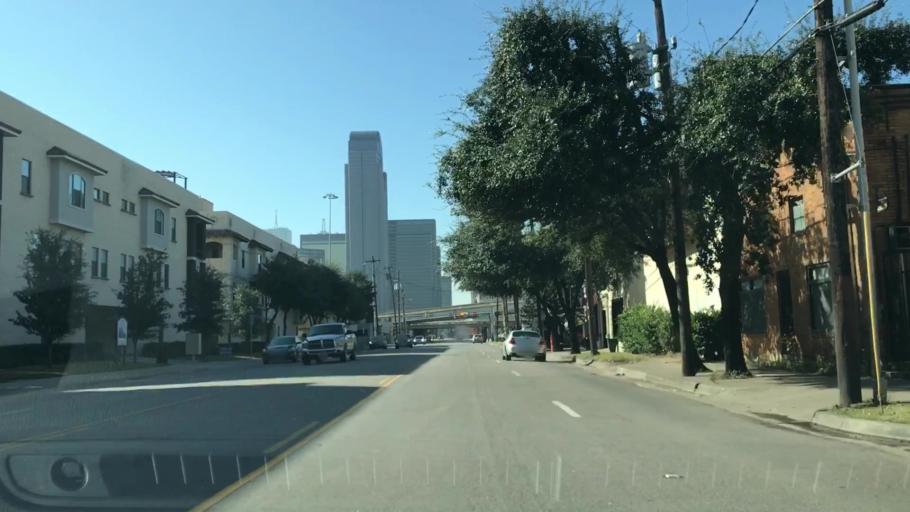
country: US
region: Texas
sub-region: Dallas County
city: Dallas
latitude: 32.7943
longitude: -96.7905
